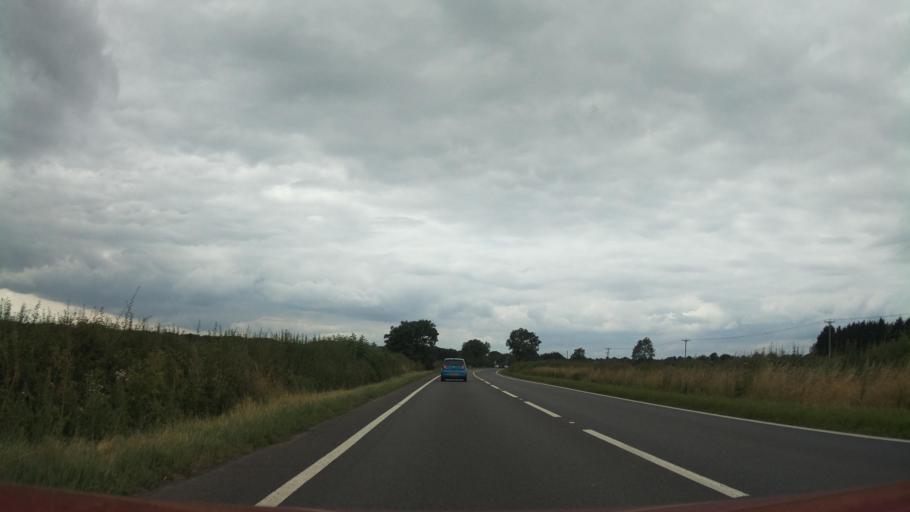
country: GB
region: England
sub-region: Lincolnshire
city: Long Bennington
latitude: 52.9340
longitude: -0.7532
